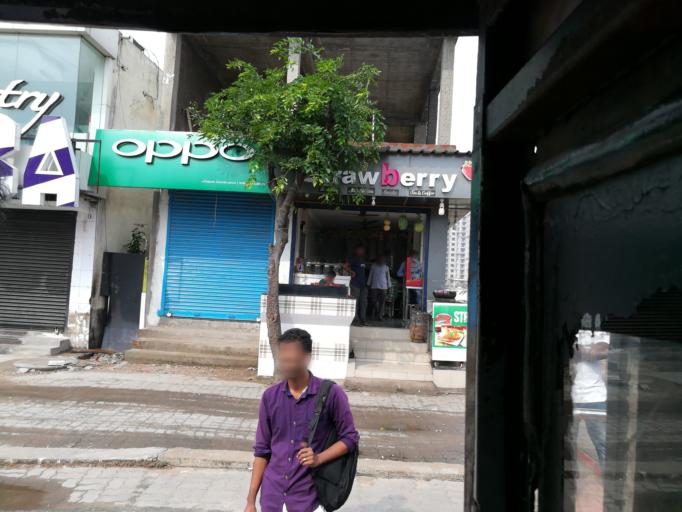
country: IN
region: Tamil Nadu
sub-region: Kancheepuram
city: Injambakkam
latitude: 12.9134
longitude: 80.2291
